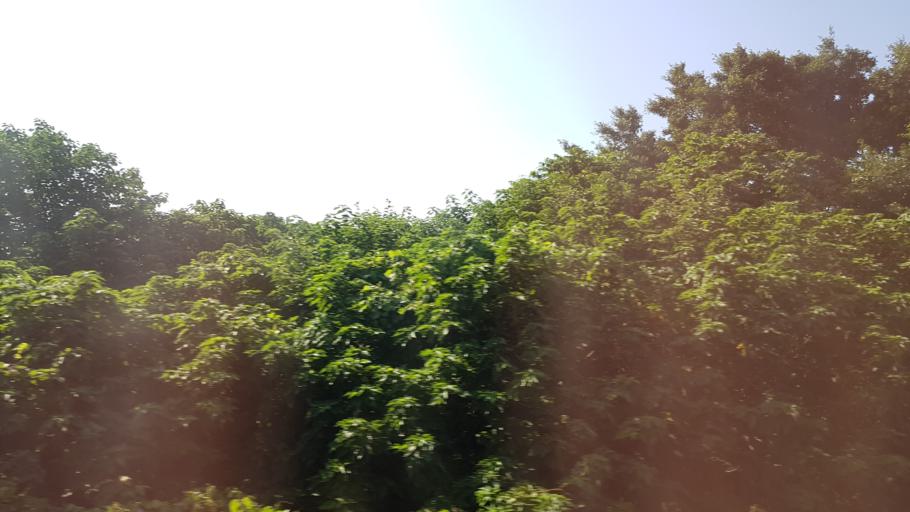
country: TW
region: Taiwan
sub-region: Miaoli
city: Miaoli
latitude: 24.6724
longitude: 120.8796
